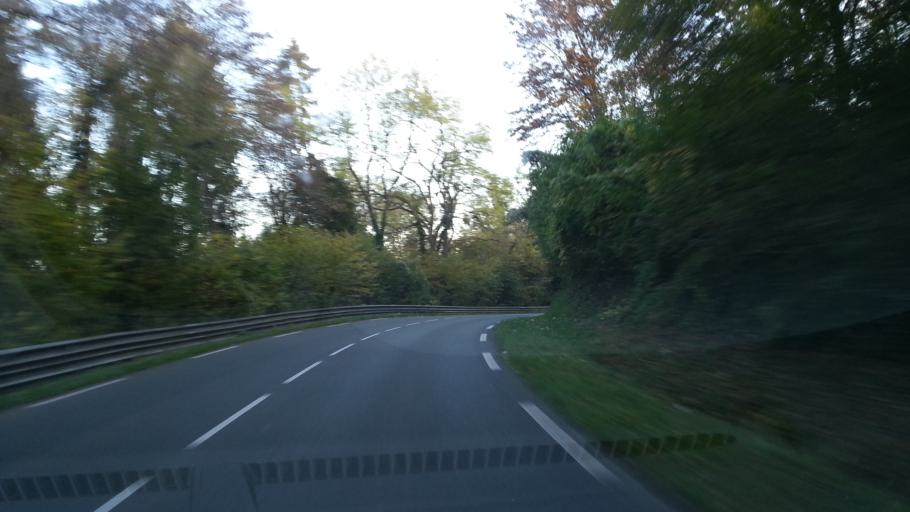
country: FR
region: Picardie
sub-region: Departement de l'Oise
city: Cires-les-Mello
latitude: 49.2845
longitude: 2.3610
